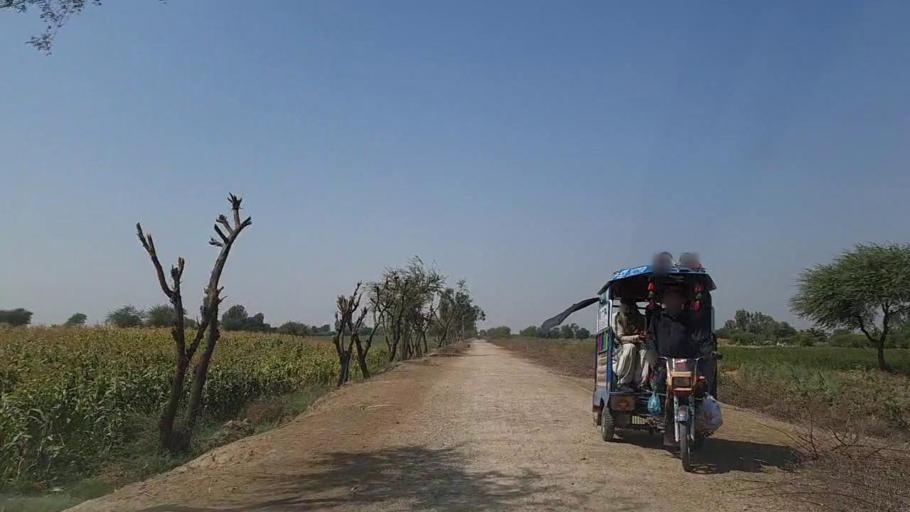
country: PK
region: Sindh
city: Samaro
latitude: 25.2248
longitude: 69.3991
